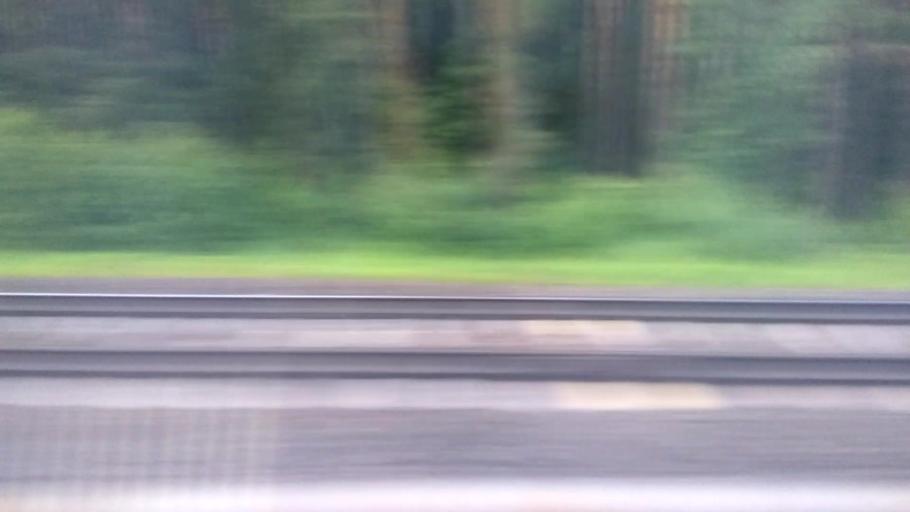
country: RU
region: Moskovskaya
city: Vostryakovo
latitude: 55.3680
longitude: 37.8254
